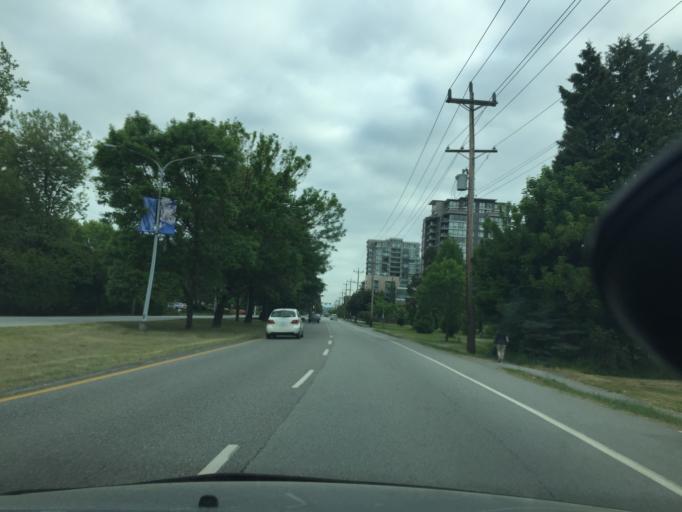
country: CA
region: British Columbia
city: Richmond
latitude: 49.1641
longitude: -123.1246
